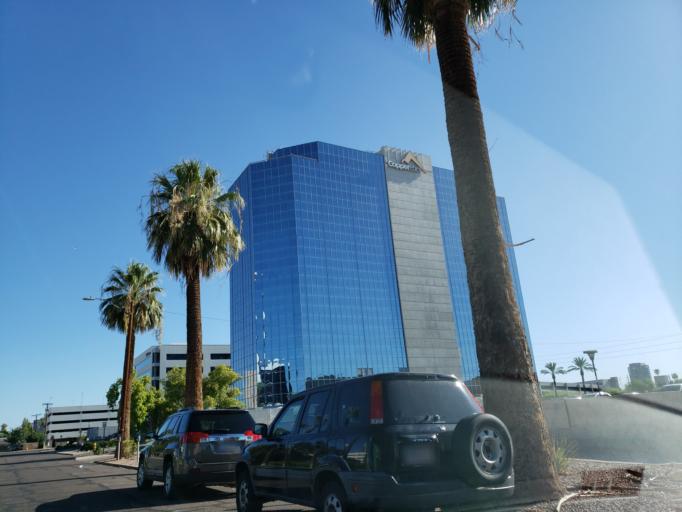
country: US
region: Arizona
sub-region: Maricopa County
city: Phoenix
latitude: 33.4825
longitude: -112.0709
